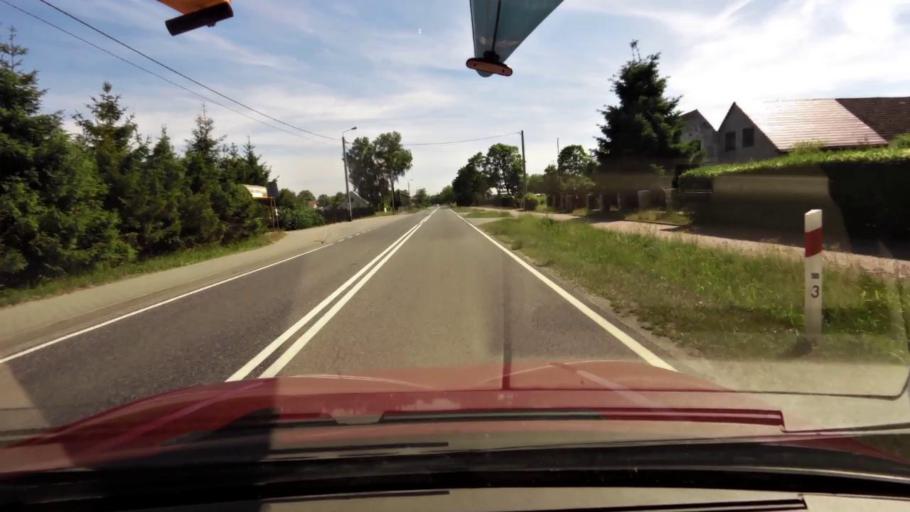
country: PL
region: Pomeranian Voivodeship
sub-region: Powiat slupski
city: Kobylnica
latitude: 54.4140
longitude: 17.0077
